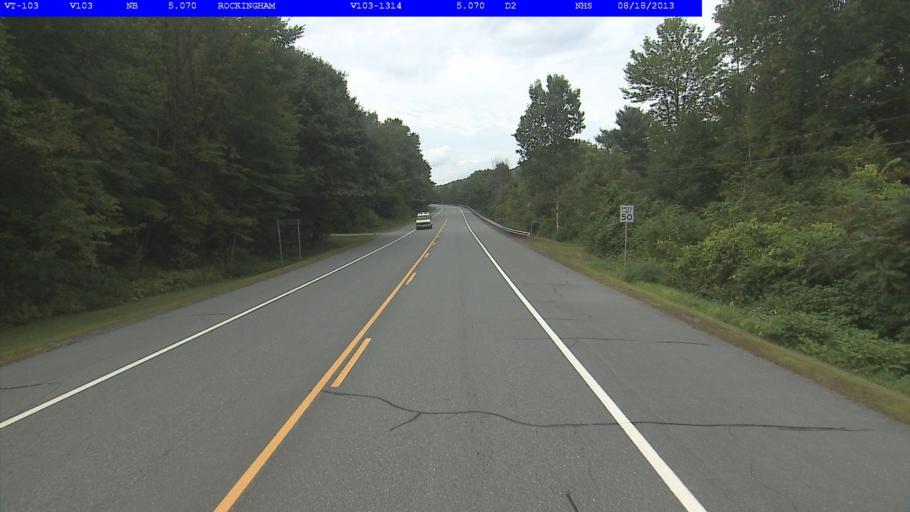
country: US
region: Vermont
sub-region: Windham County
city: Rockingham
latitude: 43.2147
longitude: -72.5382
